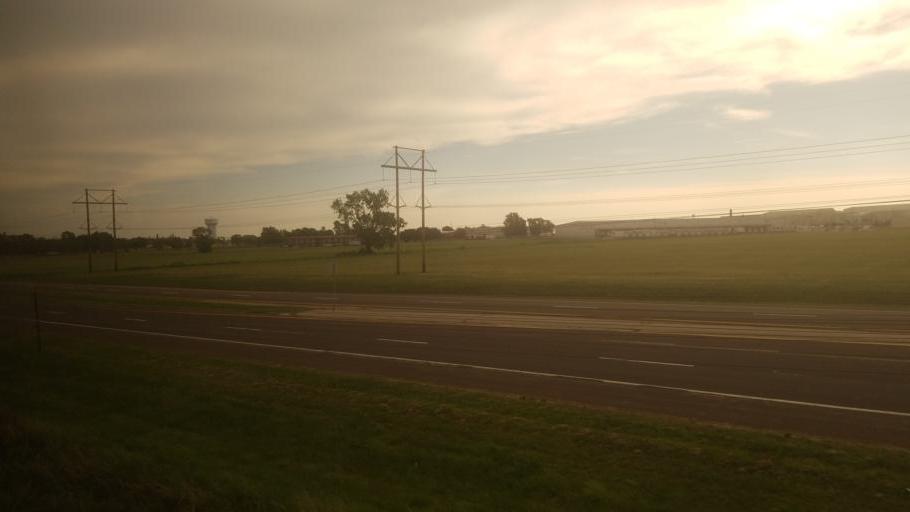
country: US
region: Kansas
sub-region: Shawnee County
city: Topeka
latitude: 38.9380
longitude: -95.6875
